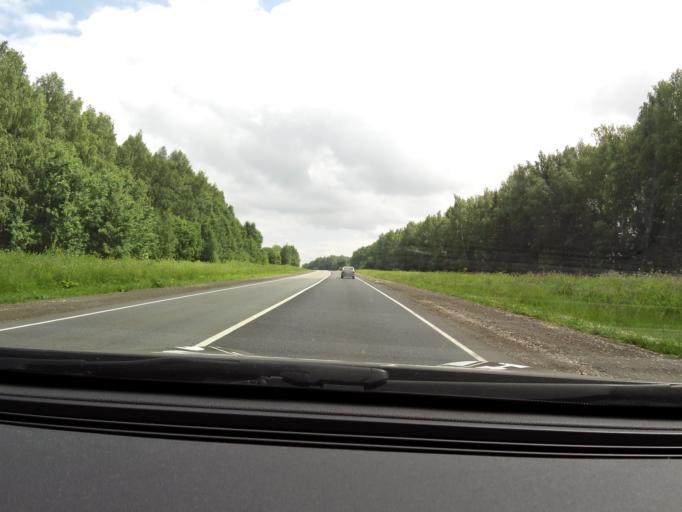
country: RU
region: Perm
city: Suksun
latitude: 57.1593
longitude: 57.2528
